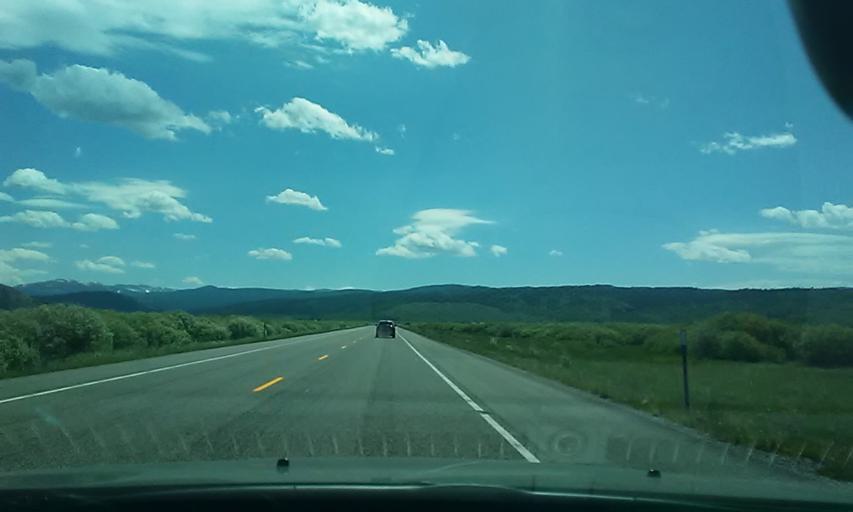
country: US
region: Wyoming
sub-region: Teton County
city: Jackson
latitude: 43.8363
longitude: -110.4337
